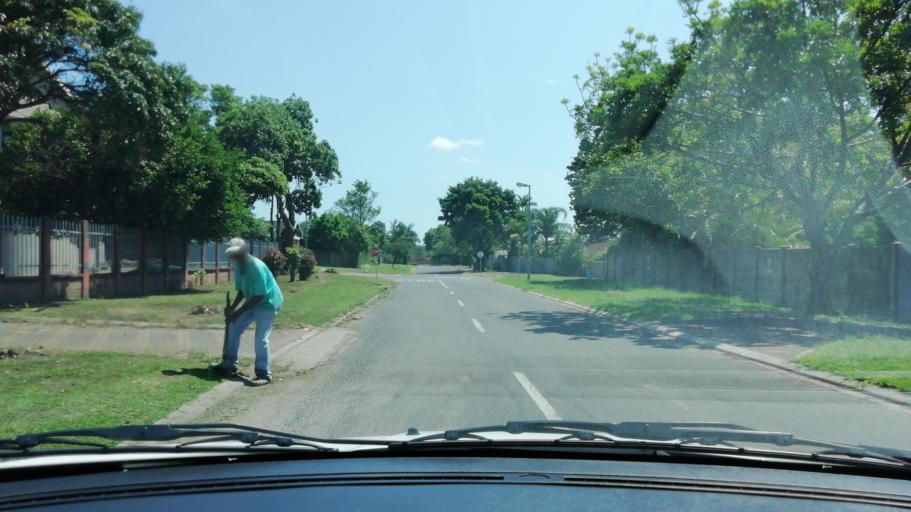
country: ZA
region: KwaZulu-Natal
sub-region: uThungulu District Municipality
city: Richards Bay
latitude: -28.7407
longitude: 32.0589
